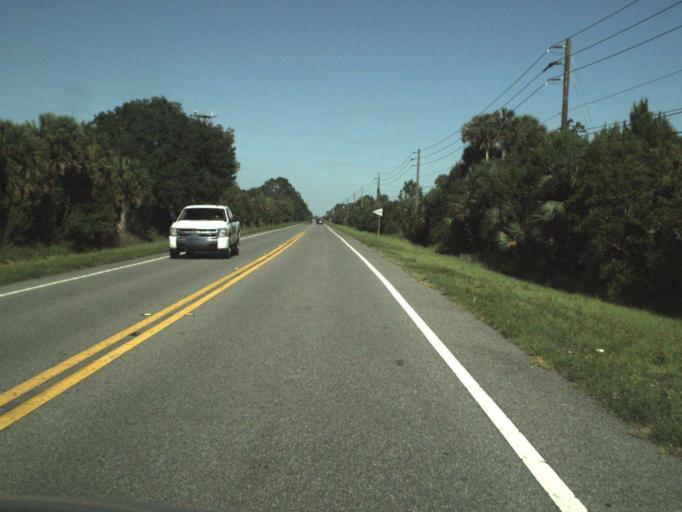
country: US
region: Florida
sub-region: Seminole County
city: Geneva
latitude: 28.7181
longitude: -81.0702
